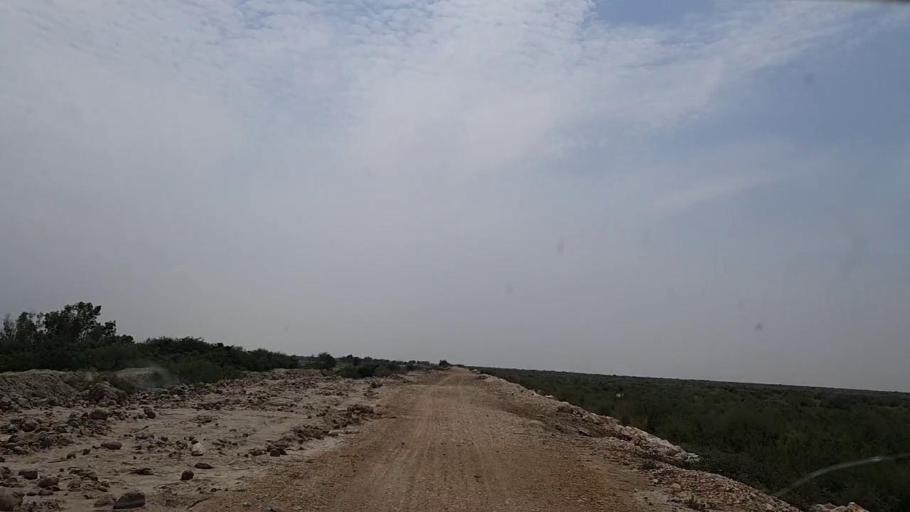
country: PK
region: Sindh
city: Phulji
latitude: 26.8589
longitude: 67.6338
